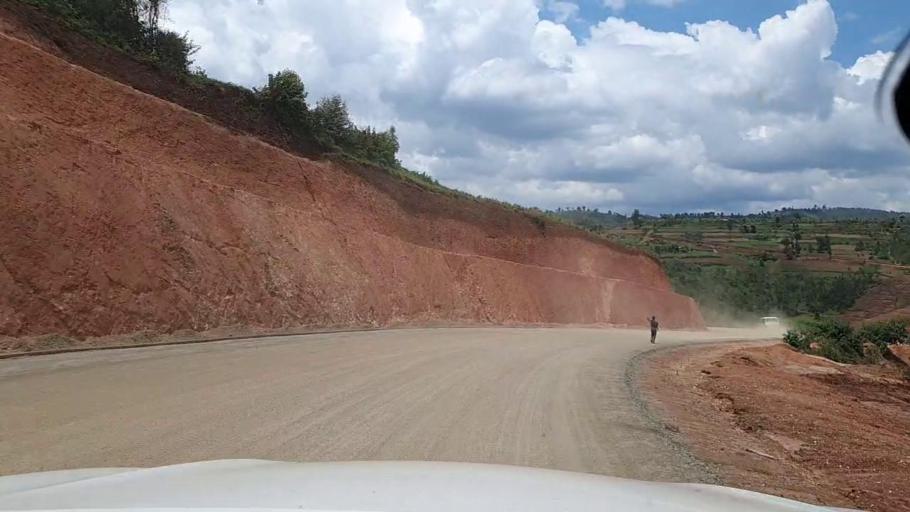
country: RW
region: Southern Province
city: Butare
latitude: -2.6947
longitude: 29.5569
